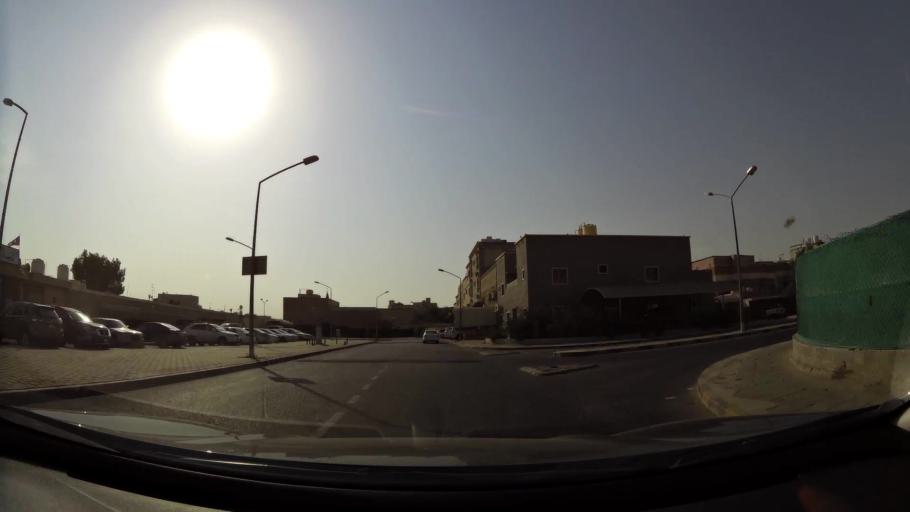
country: KW
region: Al Ahmadi
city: Ar Riqqah
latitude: 29.1585
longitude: 48.0660
